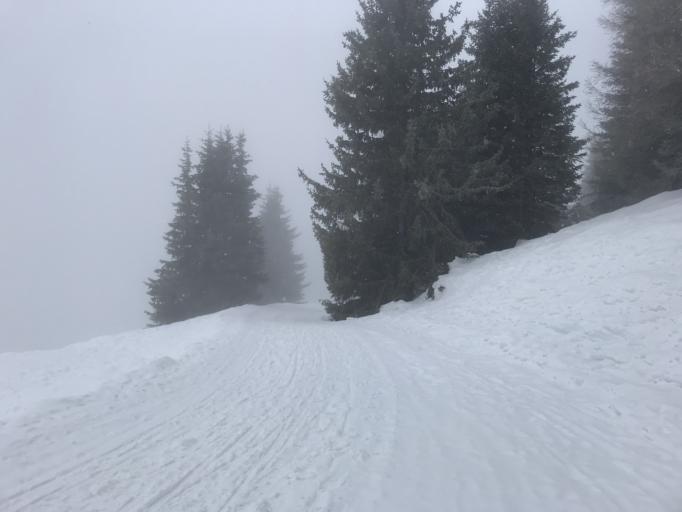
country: IT
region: Trentino-Alto Adige
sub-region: Bolzano
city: San Pietro
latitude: 46.6855
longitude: 11.7148
